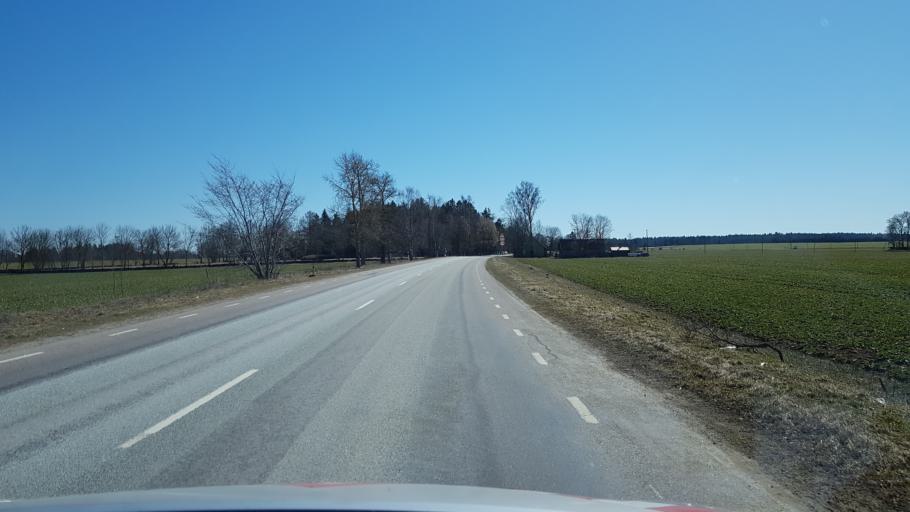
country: EE
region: Laeaene-Virumaa
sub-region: Viru-Nigula vald
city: Kunda
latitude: 59.4417
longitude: 26.6953
